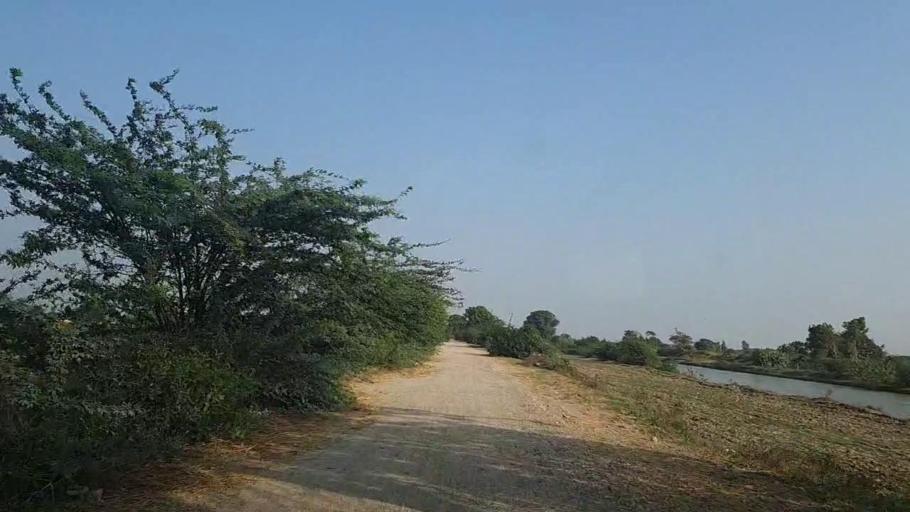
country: PK
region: Sindh
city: Mirpur Sakro
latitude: 24.5754
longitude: 67.6750
